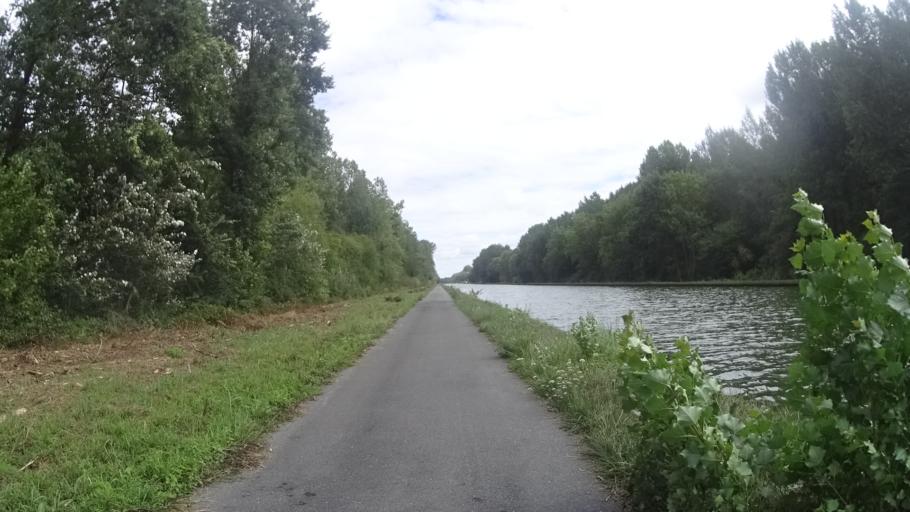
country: FR
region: Picardie
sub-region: Departement de l'Aisne
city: Blerancourt
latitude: 49.5789
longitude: 3.1279
